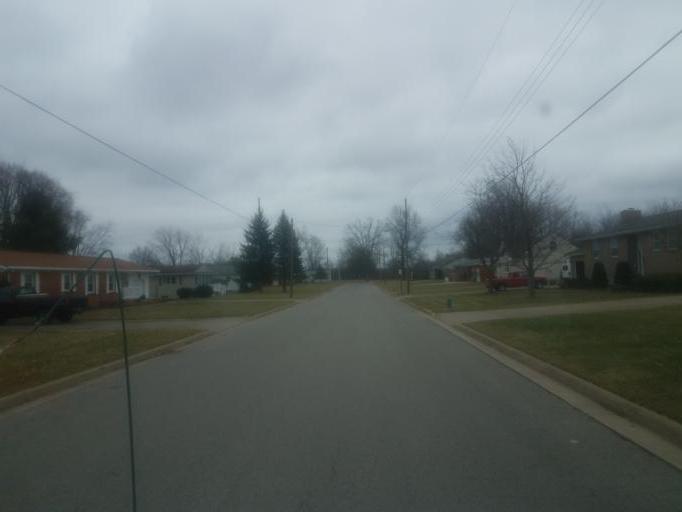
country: US
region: Ohio
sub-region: Crawford County
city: Crestline
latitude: 40.7743
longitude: -82.7340
